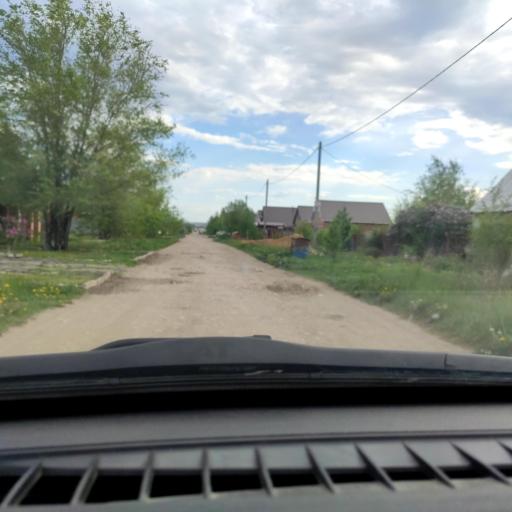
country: RU
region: Samara
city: Tol'yatti
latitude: 53.5742
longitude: 49.4119
